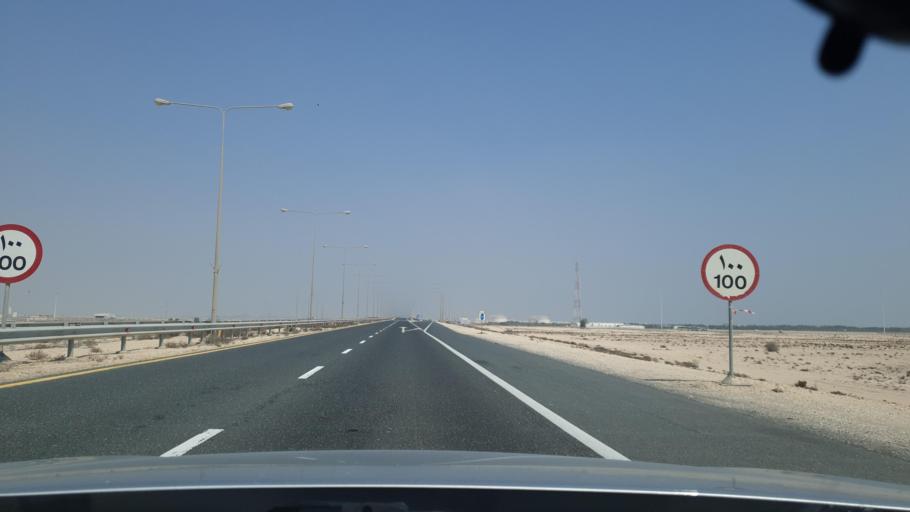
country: QA
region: Al Khawr
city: Al Khawr
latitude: 25.8349
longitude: 51.5258
